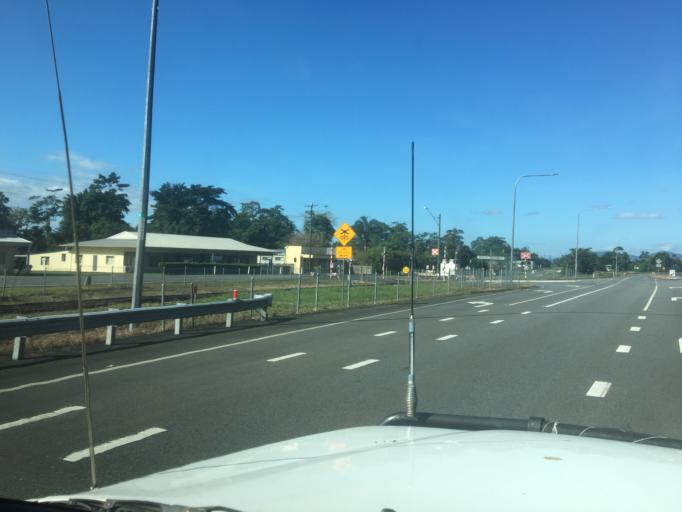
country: AU
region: Queensland
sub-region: Cassowary Coast
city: Innisfail
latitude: -17.3438
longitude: 145.9249
